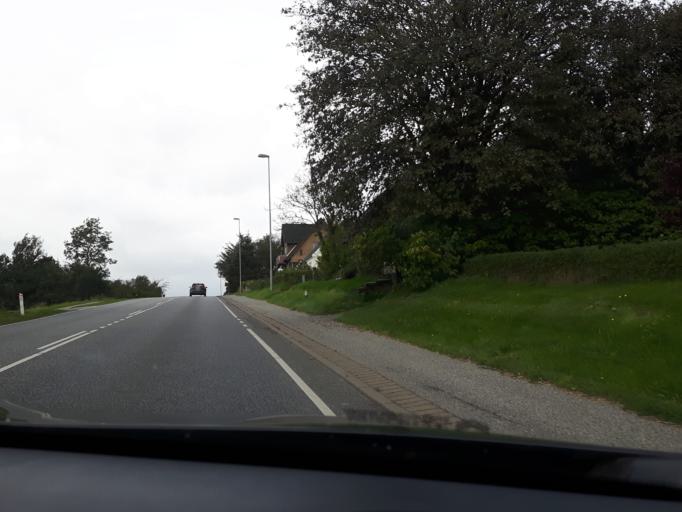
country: DK
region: North Denmark
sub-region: Jammerbugt Kommune
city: Brovst
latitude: 57.0949
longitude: 9.4739
